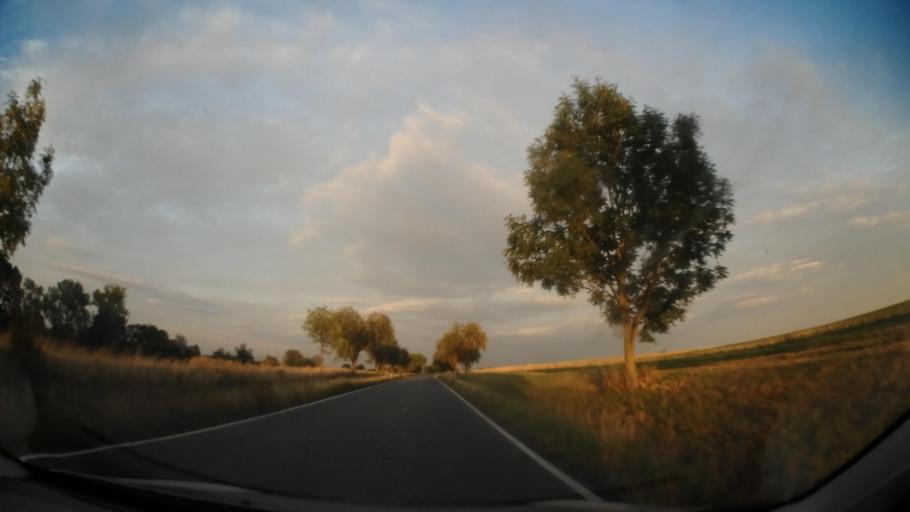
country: CZ
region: Central Bohemia
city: Loucen
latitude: 50.2383
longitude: 15.0041
